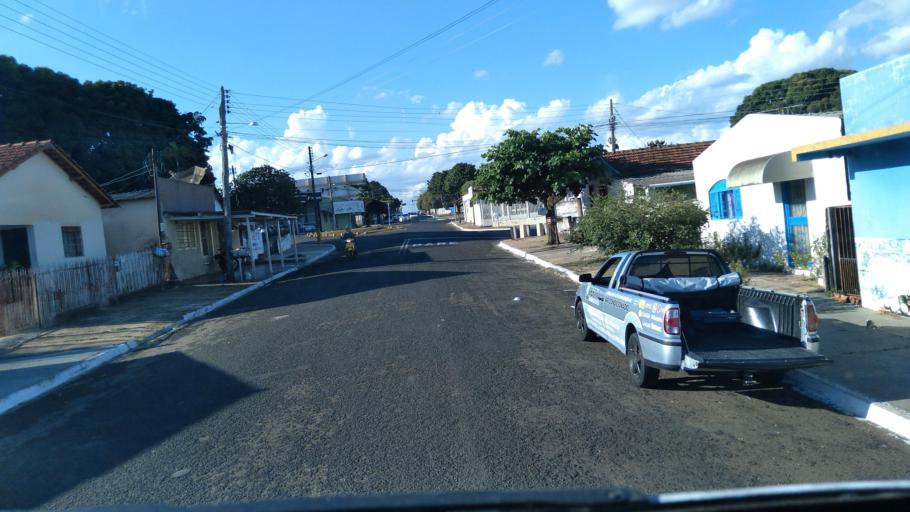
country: BR
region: Goias
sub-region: Mineiros
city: Mineiros
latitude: -17.5582
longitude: -52.5518
